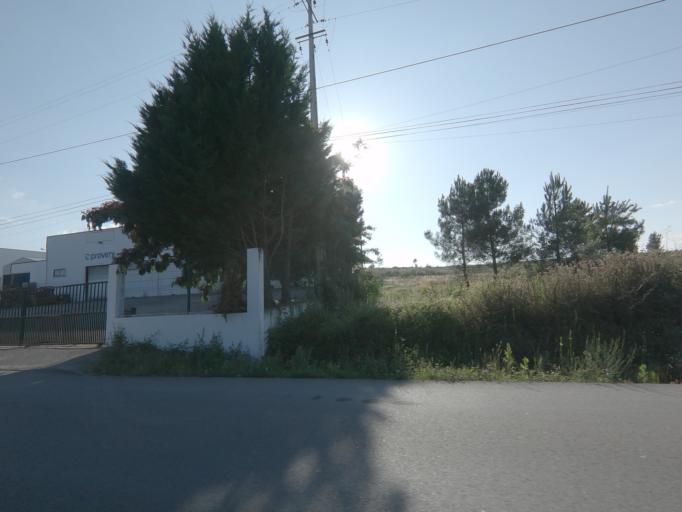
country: PT
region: Vila Real
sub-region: Chaves
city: Chaves
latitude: 41.7880
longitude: -7.4342
